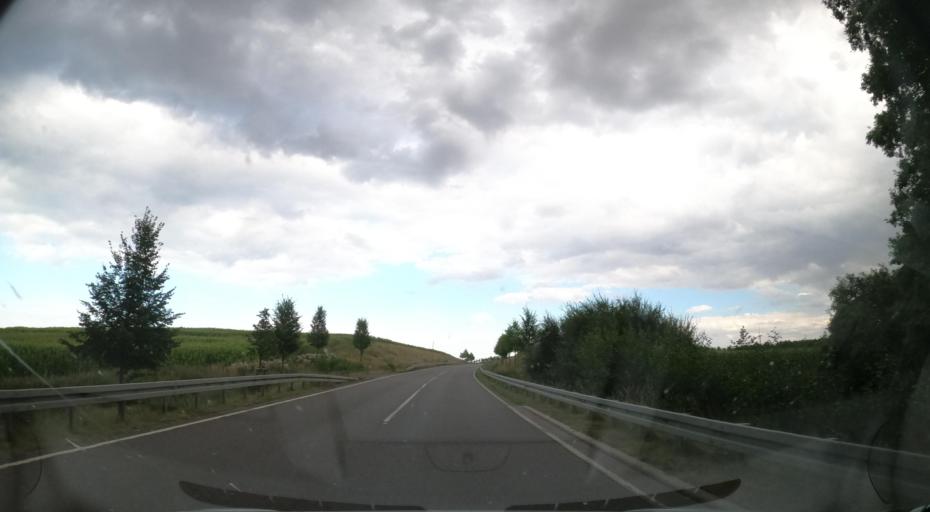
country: DE
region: Brandenburg
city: Goritz
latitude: 53.4865
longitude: 13.8516
